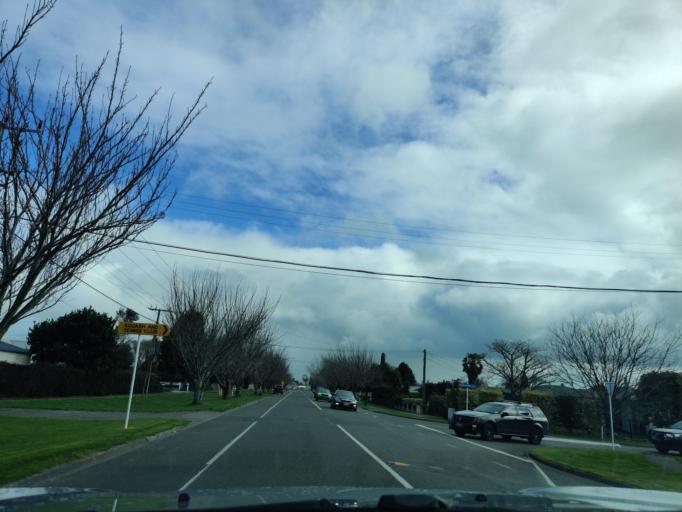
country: NZ
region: Hawke's Bay
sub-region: Hastings District
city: Hastings
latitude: -39.6714
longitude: 176.8704
